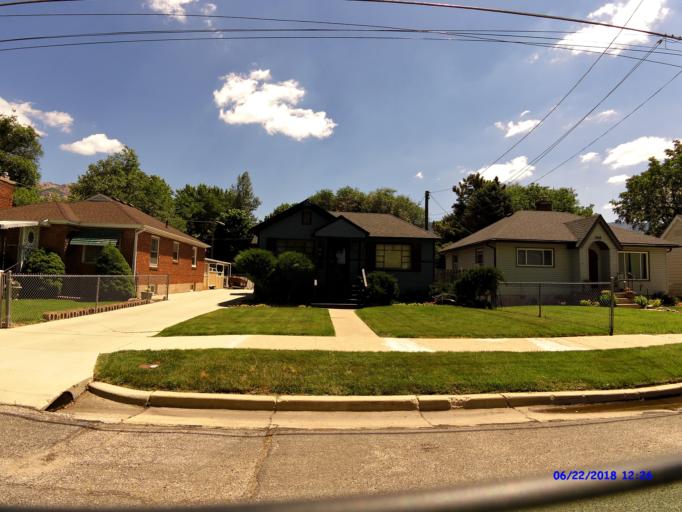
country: US
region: Utah
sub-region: Weber County
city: Ogden
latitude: 41.2401
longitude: -111.9644
